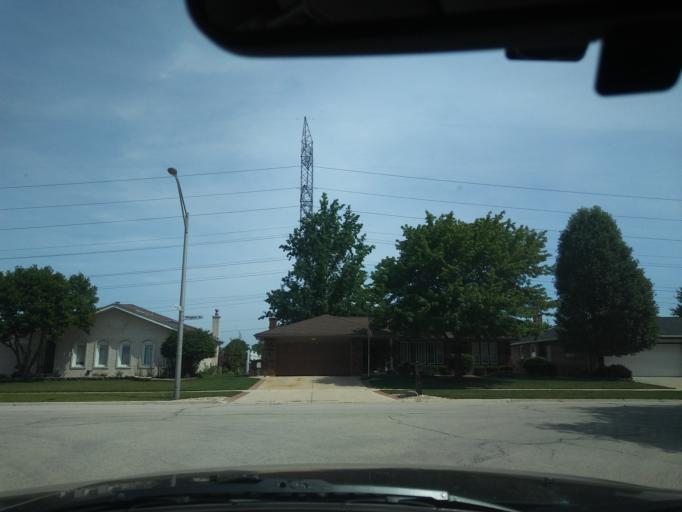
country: US
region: Illinois
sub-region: Cook County
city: Tinley Park
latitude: 41.6090
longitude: -87.8044
